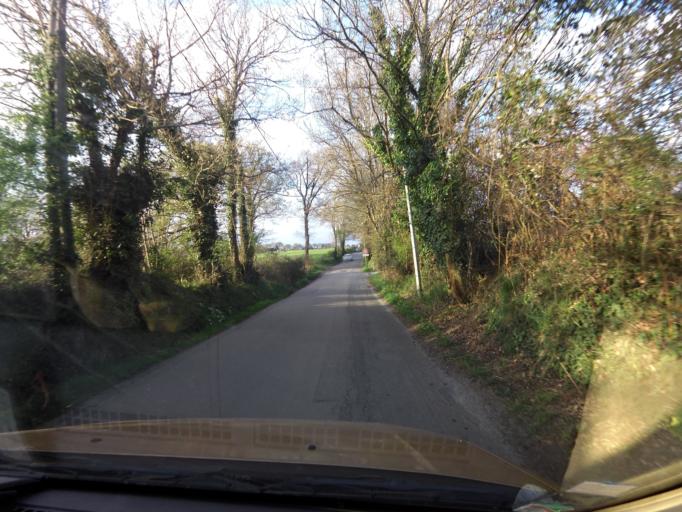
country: FR
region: Brittany
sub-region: Departement du Morbihan
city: Arradon
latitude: 47.6402
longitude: -2.8089
